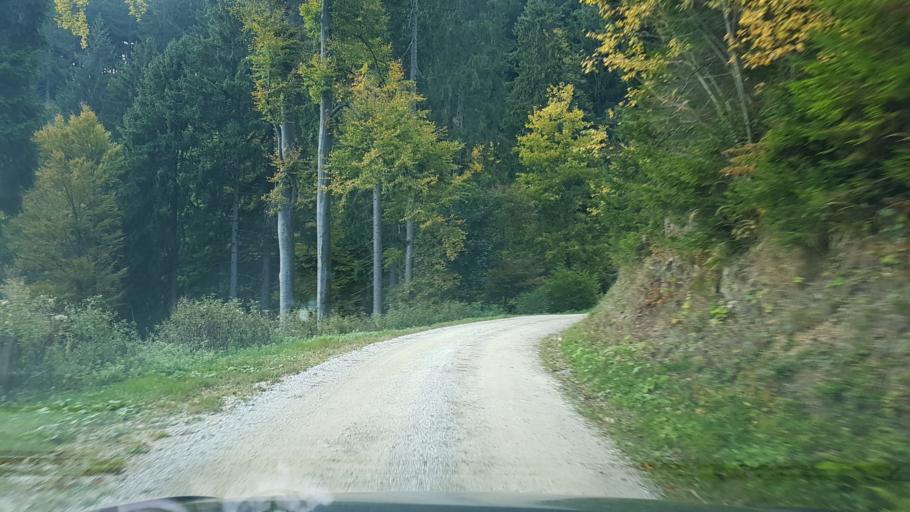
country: SI
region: Slovenj Gradec
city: Legen
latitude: 46.5255
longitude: 15.1349
